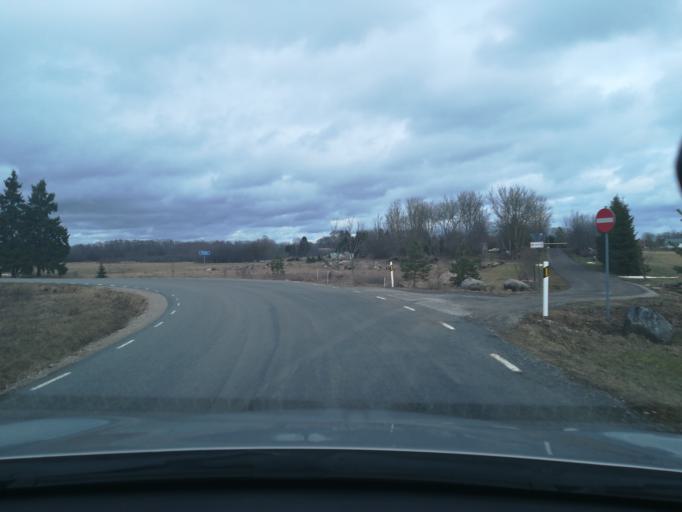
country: EE
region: Harju
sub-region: Saue linn
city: Saue
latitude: 59.3494
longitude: 24.5388
